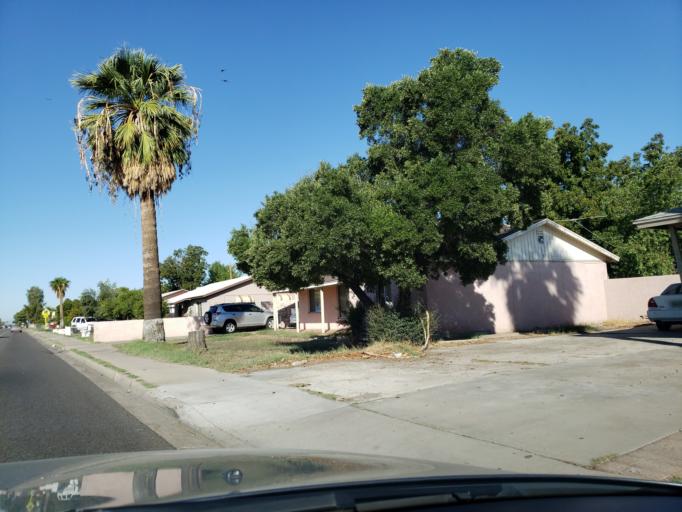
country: US
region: Arizona
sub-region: Maricopa County
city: Glendale
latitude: 33.5241
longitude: -112.1194
